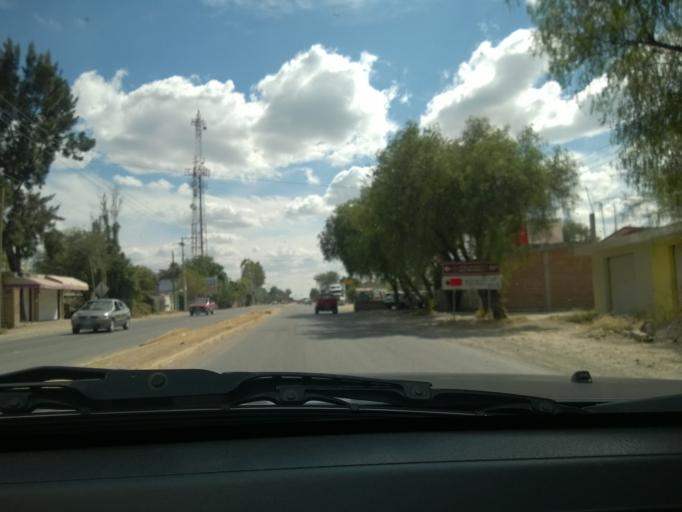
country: MX
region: Guanajuato
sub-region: Leon
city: El CERESO
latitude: 20.9796
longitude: -101.7016
